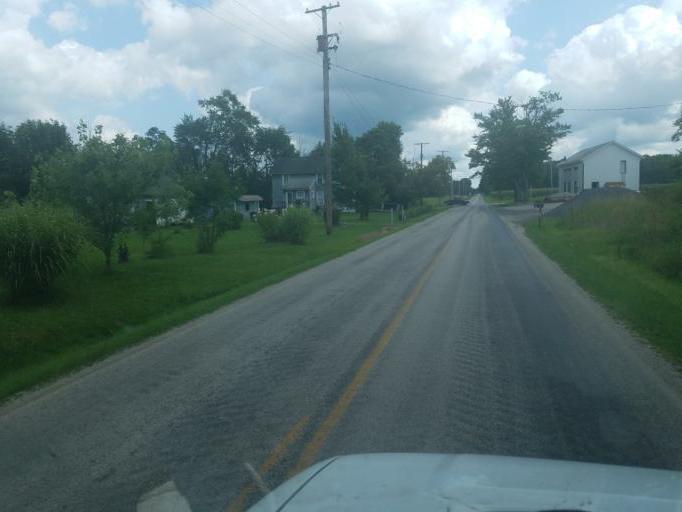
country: US
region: Ohio
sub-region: Ashtabula County
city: Roaming Shores
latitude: 41.5861
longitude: -80.7797
